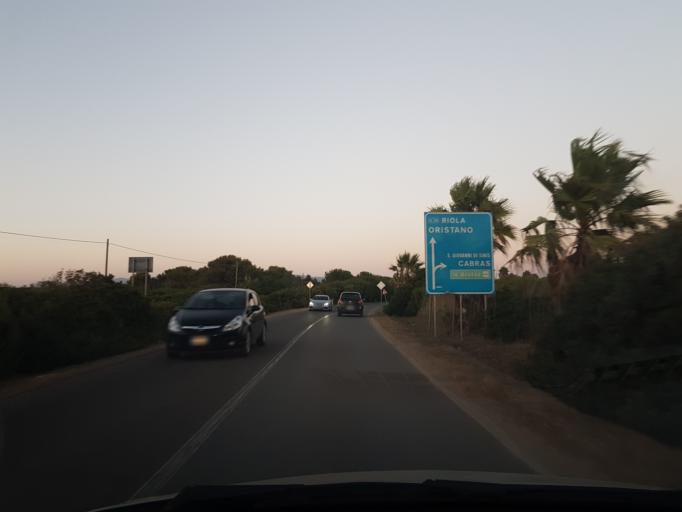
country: IT
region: Sardinia
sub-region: Provincia di Oristano
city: Riola Sardo
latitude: 40.0291
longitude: 8.4143
